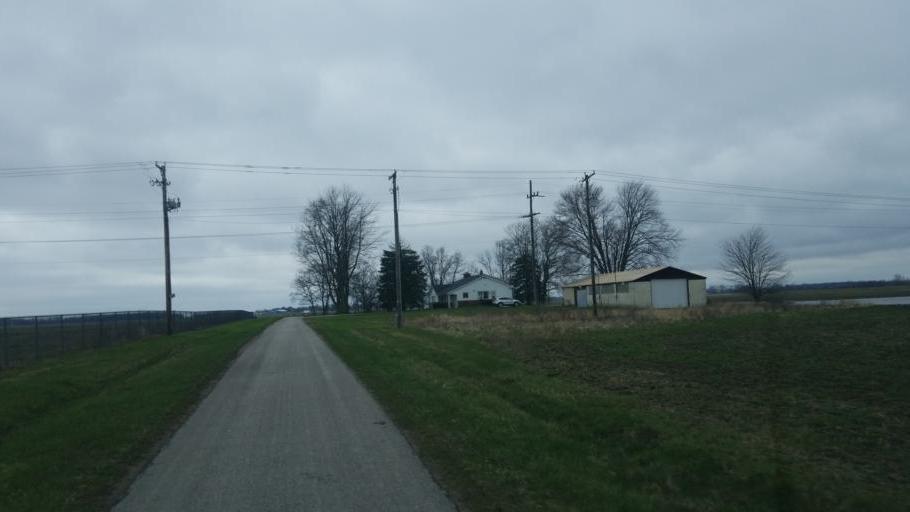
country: US
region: Ohio
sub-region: Marion County
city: Marion
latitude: 40.6156
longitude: -83.0507
